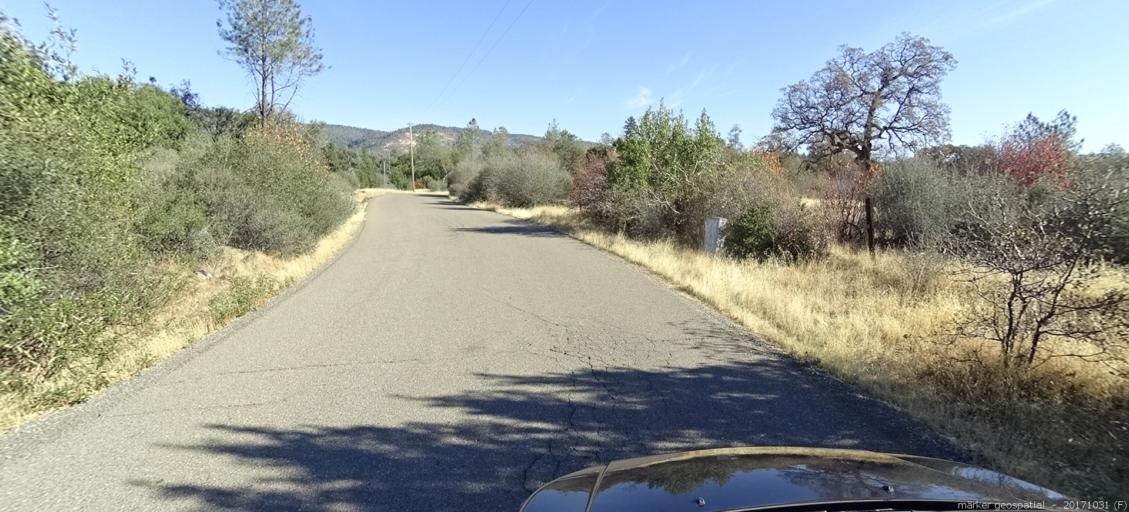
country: US
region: California
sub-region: Shasta County
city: Shingletown
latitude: 40.4435
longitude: -121.8703
